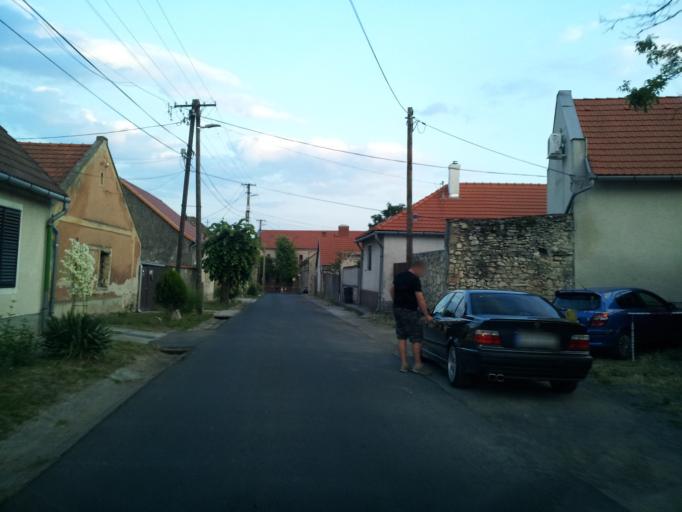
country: HU
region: Veszprem
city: Tapolca
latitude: 46.8841
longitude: 17.4436
